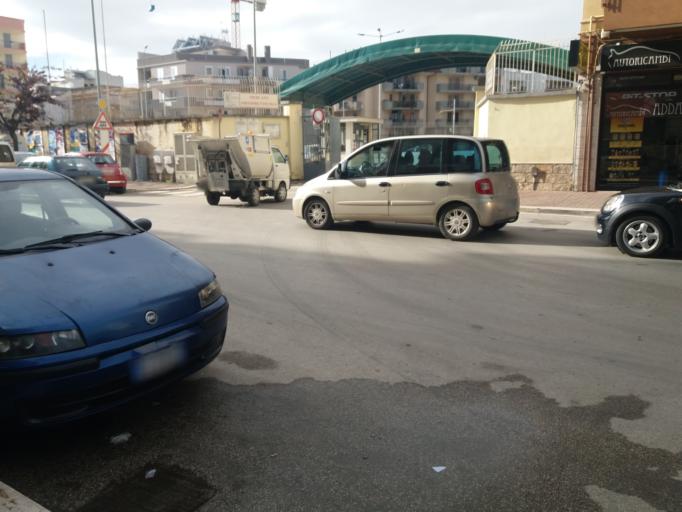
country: IT
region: Apulia
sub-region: Provincia di Barletta - Andria - Trani
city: Andria
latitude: 41.2360
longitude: 16.2947
